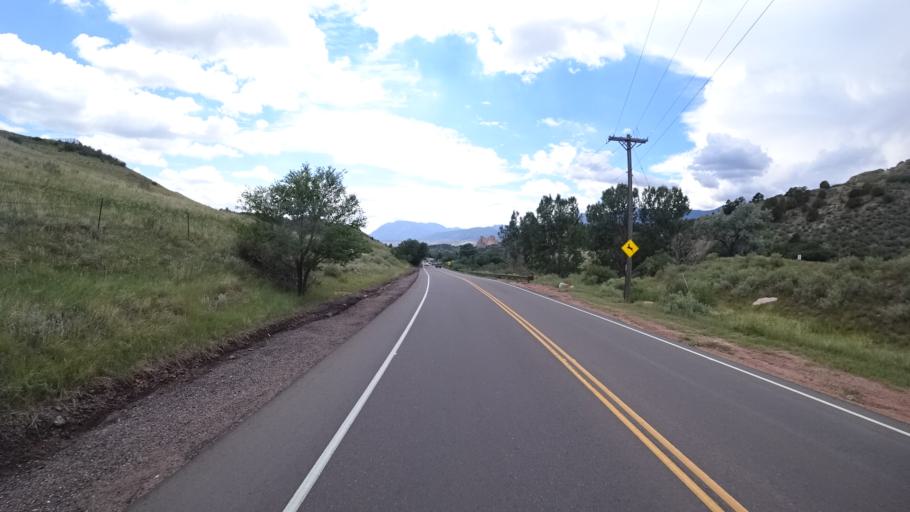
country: US
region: Colorado
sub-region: El Paso County
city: Manitou Springs
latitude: 38.8944
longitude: -104.8754
